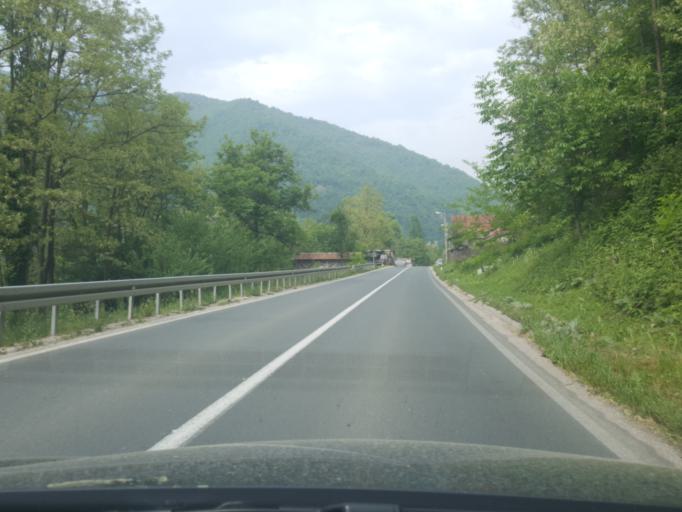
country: RS
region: Central Serbia
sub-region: Zlatiborski Okrug
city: Bajina Basta
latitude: 44.0069
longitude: 19.5951
